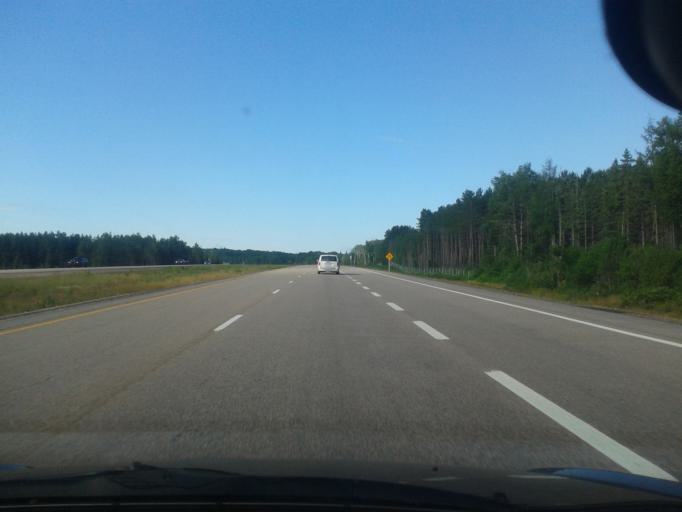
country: CA
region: Ontario
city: South River
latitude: 45.8131
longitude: -79.4055
